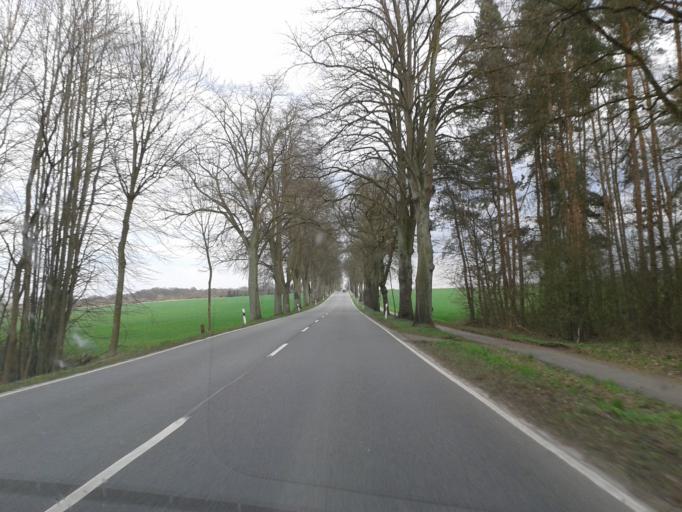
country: DE
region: Saxony-Anhalt
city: Wallstawe
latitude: 52.8785
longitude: 11.0479
